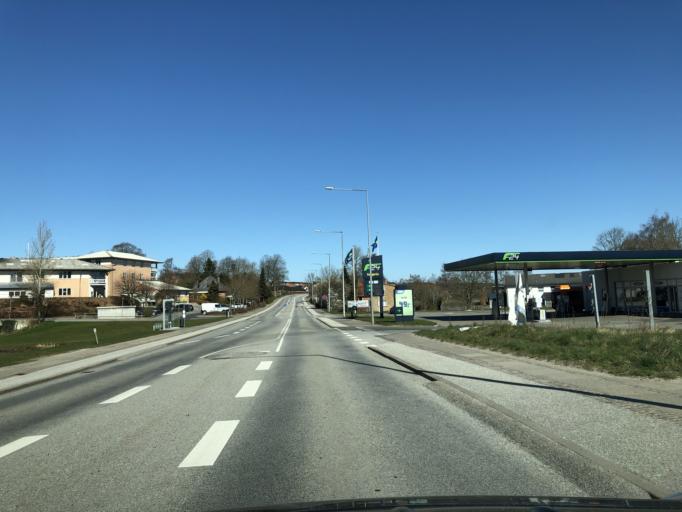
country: DK
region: North Denmark
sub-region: Rebild Kommune
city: Stovring
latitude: 56.8837
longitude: 9.8395
